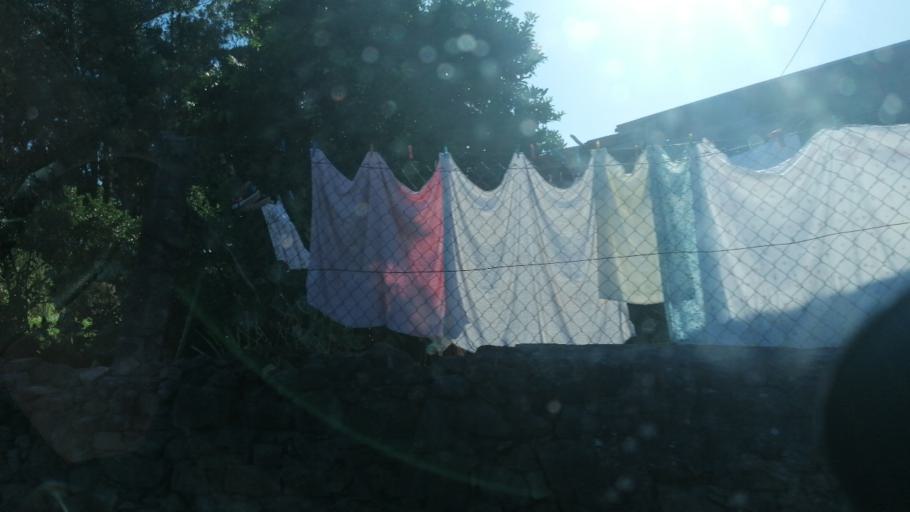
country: PT
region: Porto
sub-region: Santo Tirso
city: Sao Miguel do Couto
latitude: 41.2938
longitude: -8.4711
